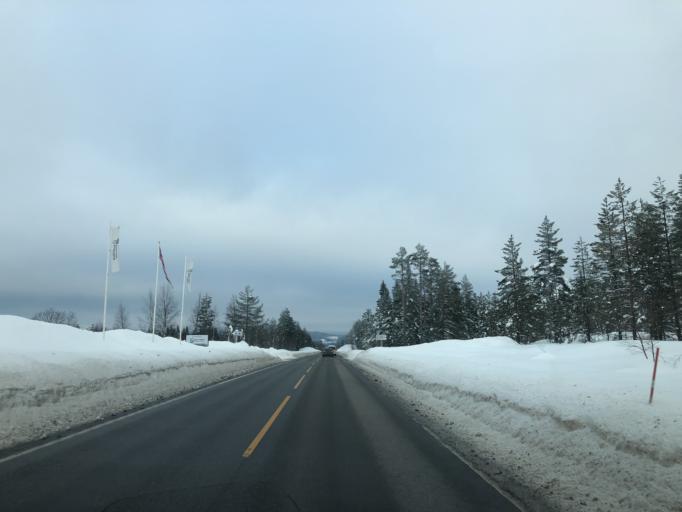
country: NO
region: Hedmark
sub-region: Trysil
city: Innbygda
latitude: 61.2351
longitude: 12.2596
